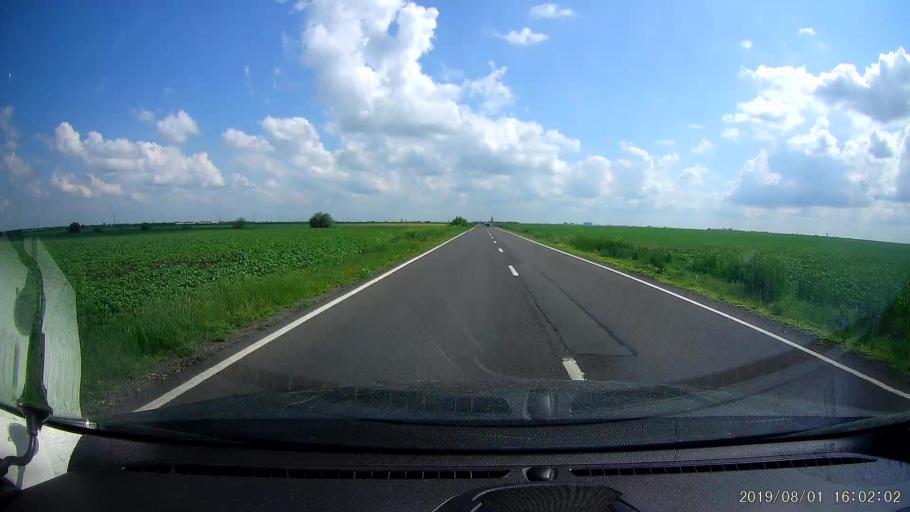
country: RO
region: Ialomita
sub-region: Comuna Ciulnita
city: Ciulnita
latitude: 44.4976
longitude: 27.3887
